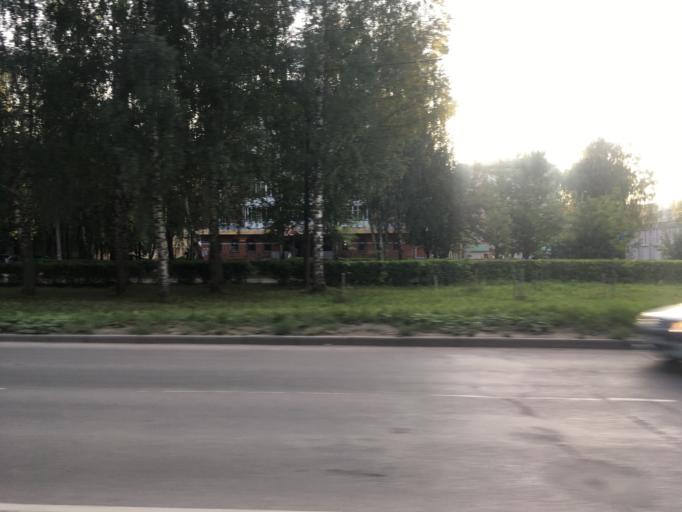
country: RU
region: Mariy-El
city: Yoshkar-Ola
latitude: 56.6496
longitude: 47.8748
